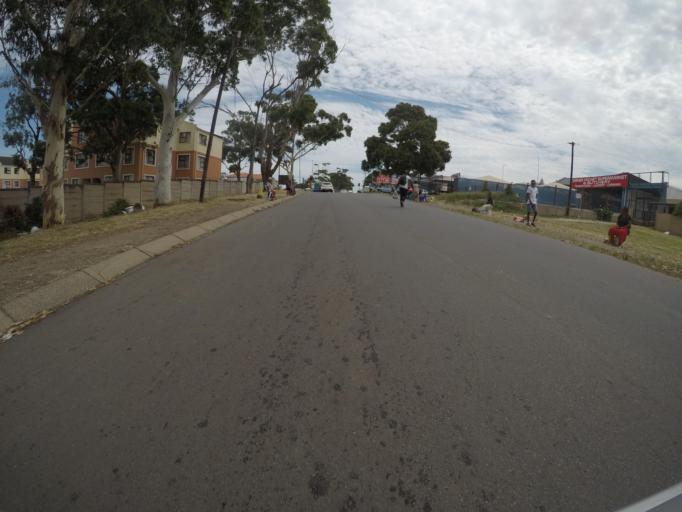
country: ZA
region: Eastern Cape
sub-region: Buffalo City Metropolitan Municipality
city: East London
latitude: -32.9968
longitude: 27.8762
